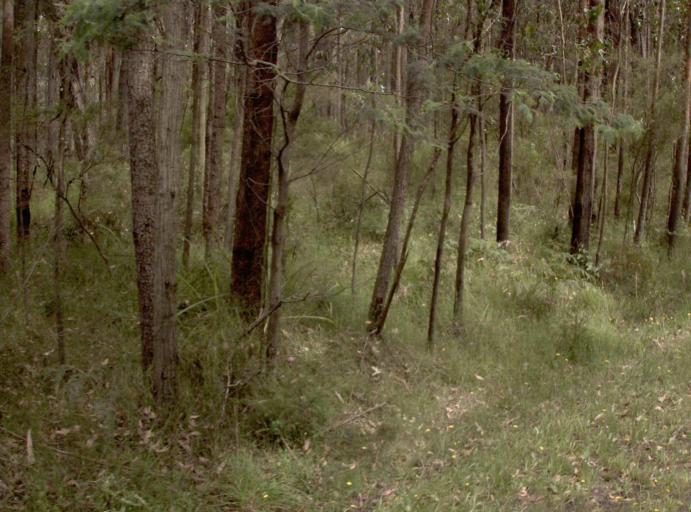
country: AU
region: Victoria
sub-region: Latrobe
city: Moe
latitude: -37.9958
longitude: 146.4105
